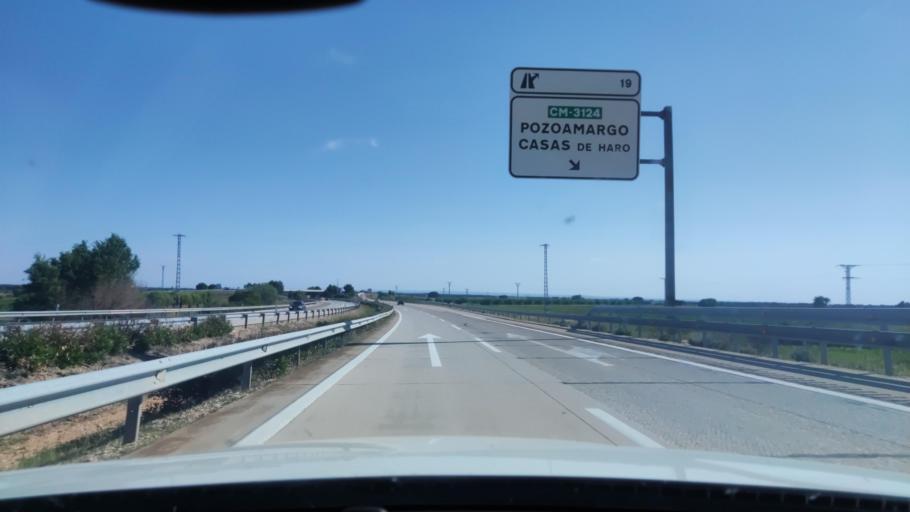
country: ES
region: Castille-La Mancha
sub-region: Provincia de Cuenca
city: Pozoamargo
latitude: 39.3646
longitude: -2.2033
